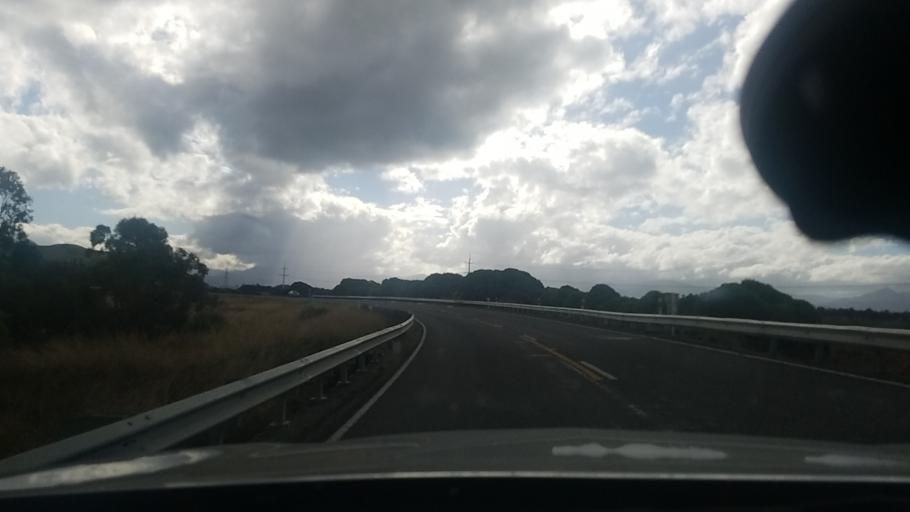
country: NZ
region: Marlborough
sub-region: Marlborough District
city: Blenheim
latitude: -41.5448
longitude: 174.0406
